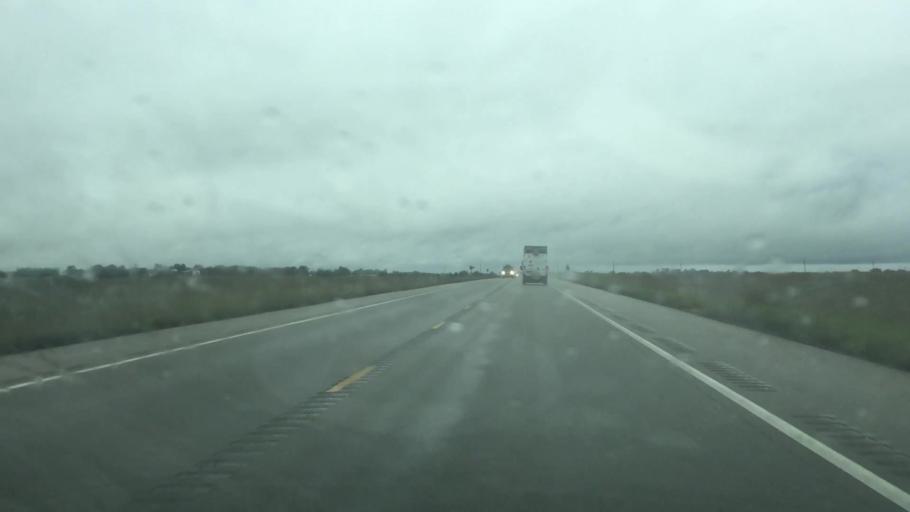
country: US
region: Kansas
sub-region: Allen County
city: Iola
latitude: 38.0855
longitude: -95.3671
